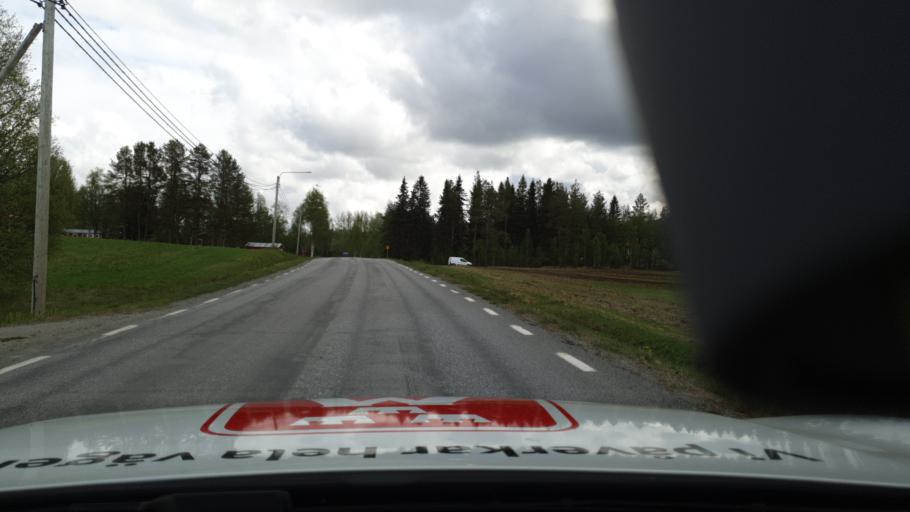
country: SE
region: Vaesterbotten
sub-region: Vilhelmina Kommun
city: Sjoberg
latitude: 64.6412
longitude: 16.3575
